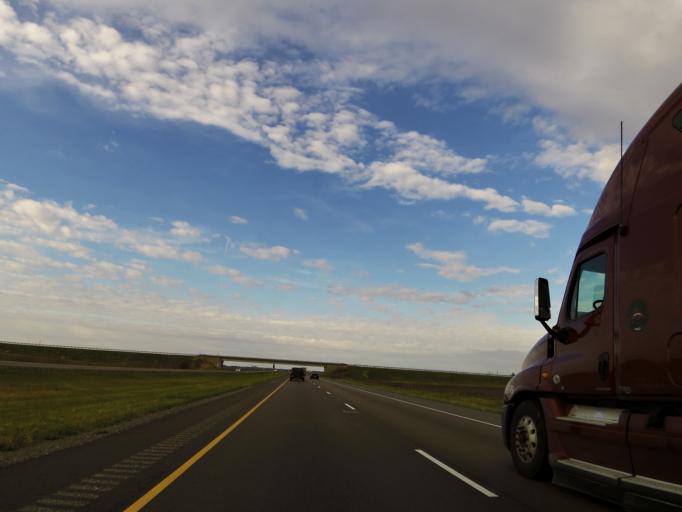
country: US
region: Illinois
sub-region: Washington County
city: Okawville
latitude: 38.4278
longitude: -89.4746
